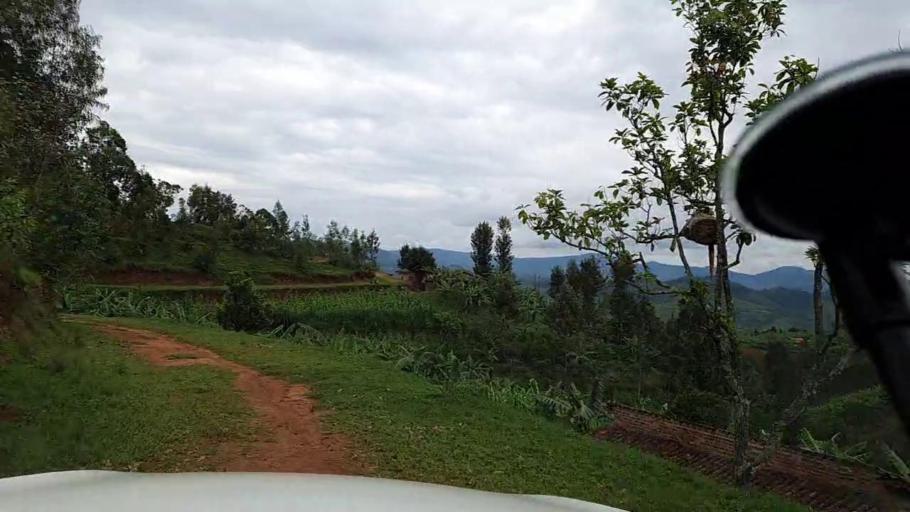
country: RW
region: Southern Province
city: Gitarama
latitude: -2.0841
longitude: 29.6483
